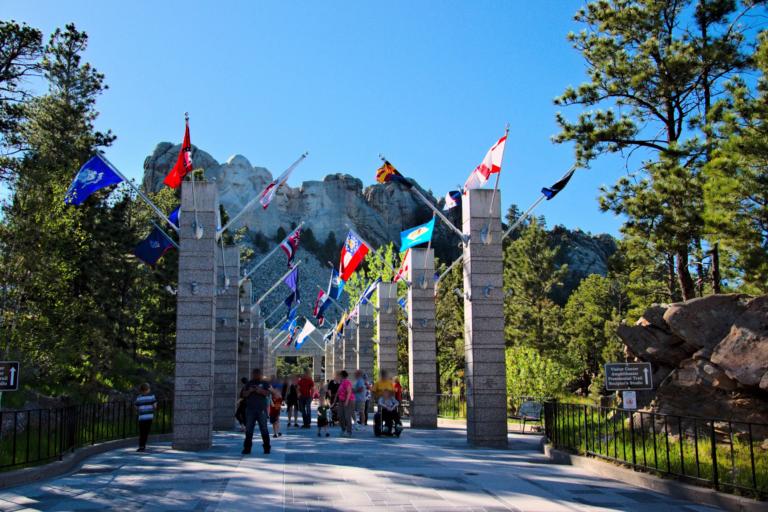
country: US
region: South Dakota
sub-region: Custer County
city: Custer
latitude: 43.8766
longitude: -103.4553
